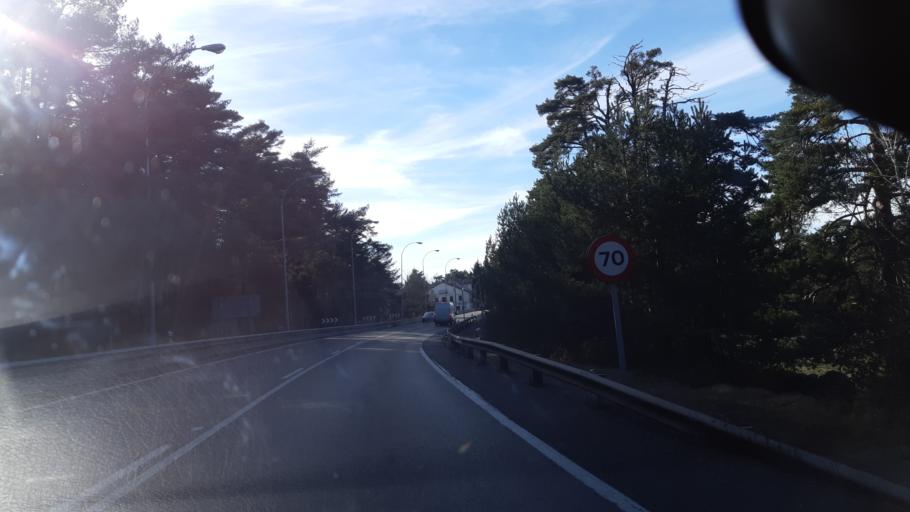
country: ES
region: Madrid
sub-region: Provincia de Madrid
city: Guadarrama
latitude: 40.7107
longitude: -4.1756
